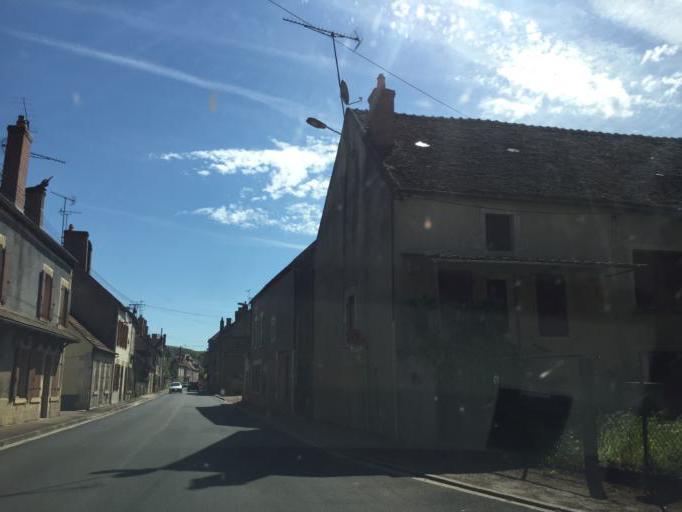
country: FR
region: Bourgogne
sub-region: Departement de la Nievre
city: Clamecy
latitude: 47.4353
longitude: 3.5824
